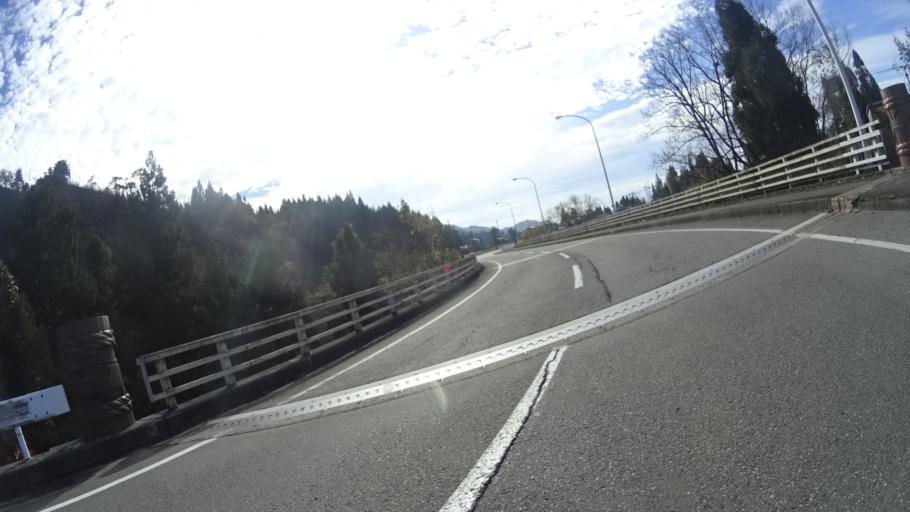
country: JP
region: Niigata
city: Tochio-honcho
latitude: 37.3030
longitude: 139.0020
